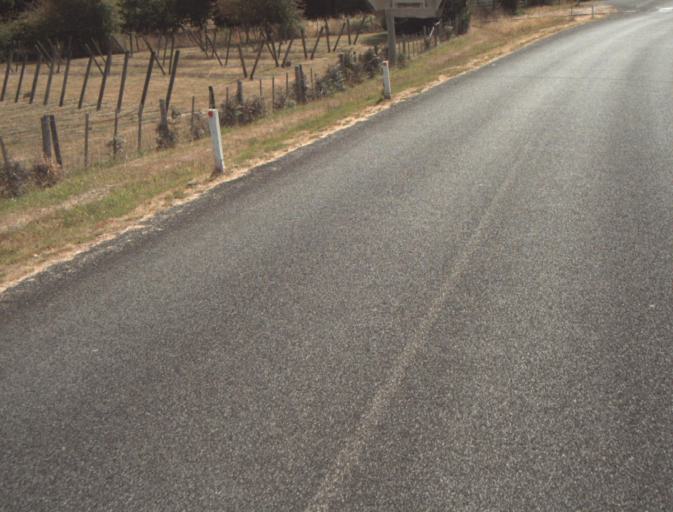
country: AU
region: Tasmania
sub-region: Launceston
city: Mayfield
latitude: -41.2574
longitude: 147.1938
